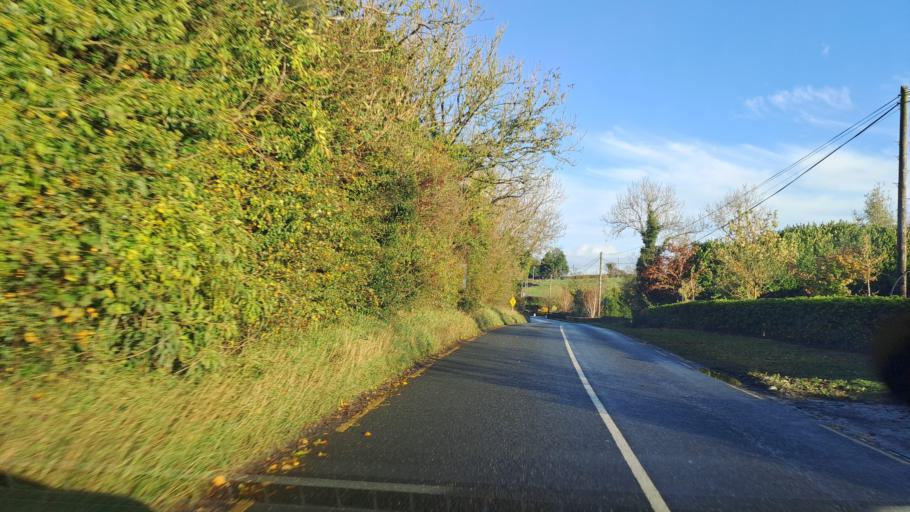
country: IE
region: Ulster
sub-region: County Monaghan
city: Monaghan
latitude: 54.2046
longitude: -6.9864
